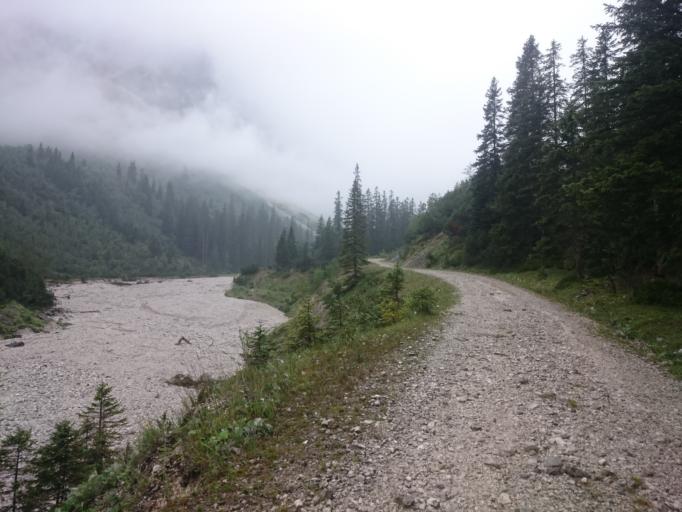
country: AT
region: Tyrol
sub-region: Politischer Bezirk Innsbruck Land
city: Thaur
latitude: 47.4161
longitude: 11.4731
